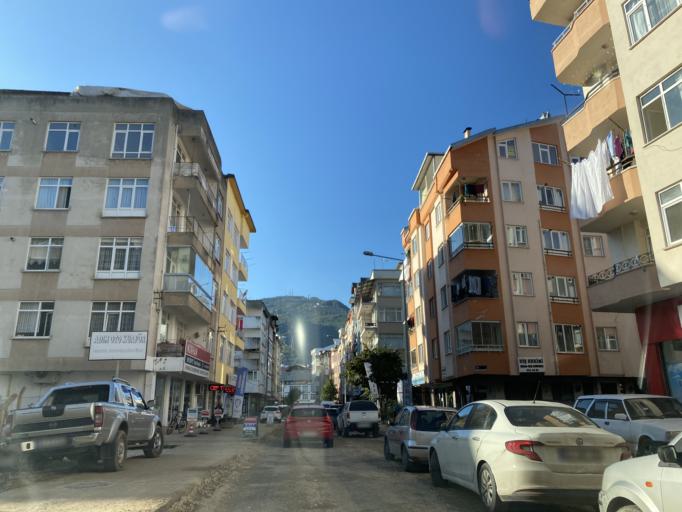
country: TR
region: Ordu
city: Ordu
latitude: 40.9822
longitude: 37.8866
